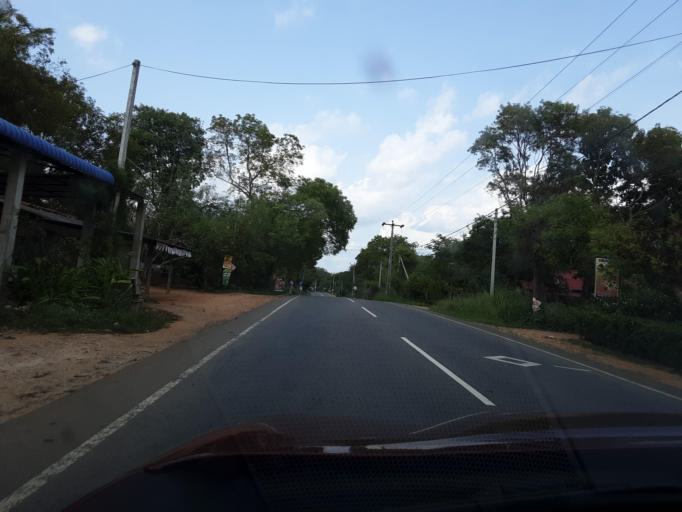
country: LK
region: Uva
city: Haputale
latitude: 6.5335
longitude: 81.1322
